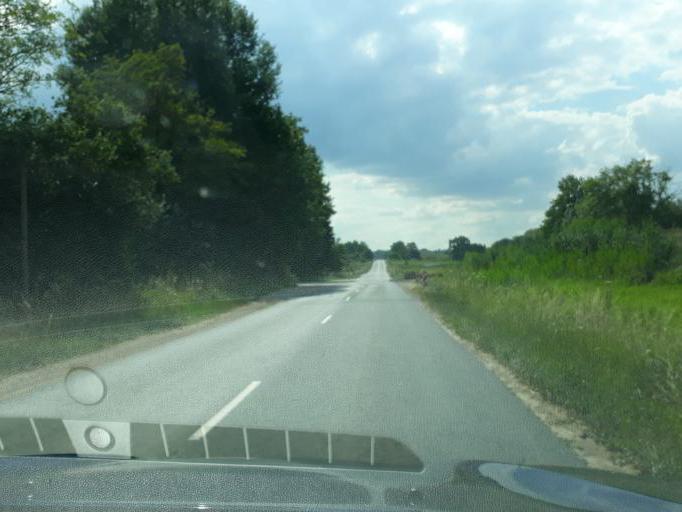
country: FR
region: Centre
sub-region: Departement du Cher
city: Cours-les-Barres
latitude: 47.0123
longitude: 3.0475
